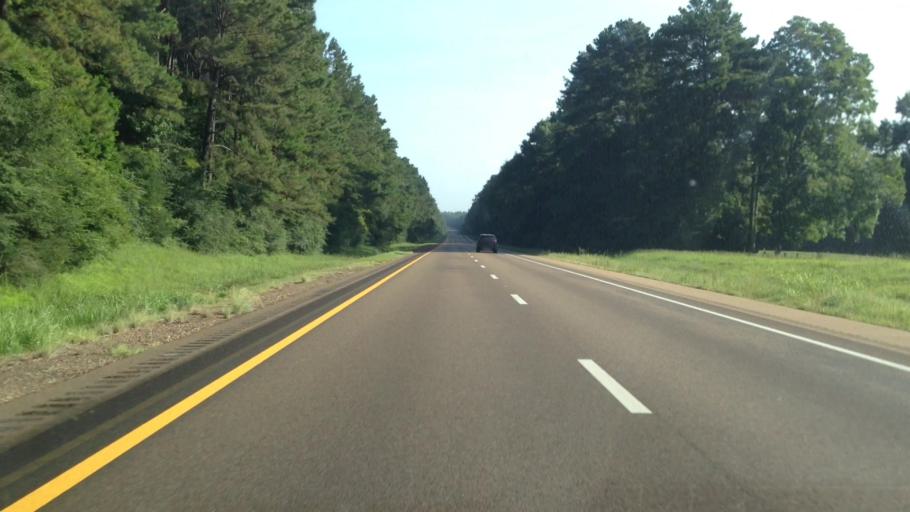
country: US
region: Mississippi
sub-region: Pike County
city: Summit
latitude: 31.3147
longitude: -90.4776
